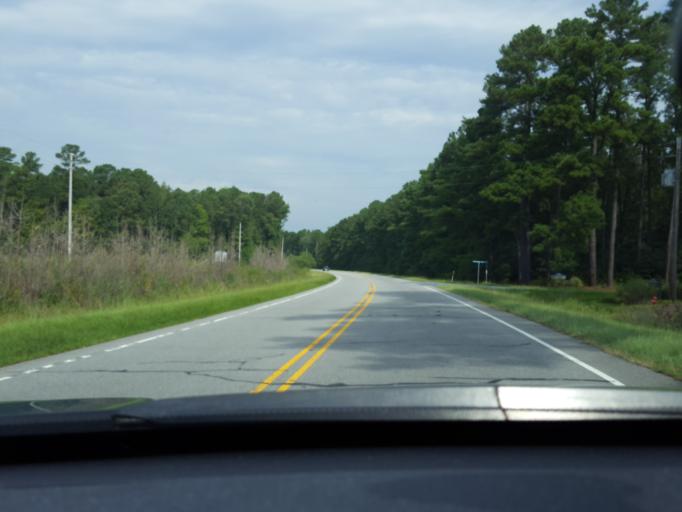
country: US
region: North Carolina
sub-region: Washington County
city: Plymouth
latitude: 35.9650
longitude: -76.7496
